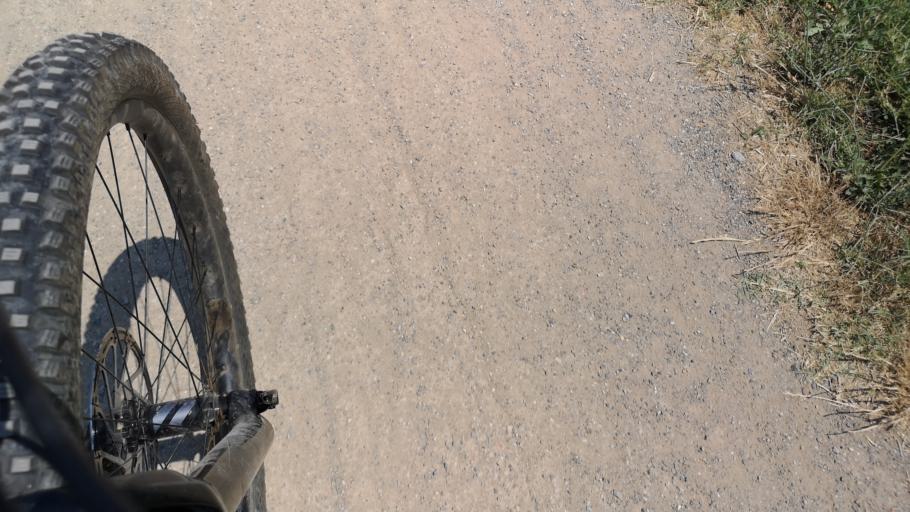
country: IT
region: Tuscany
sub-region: Provincia di Pistoia
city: Catena
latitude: 43.8581
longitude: 11.0331
